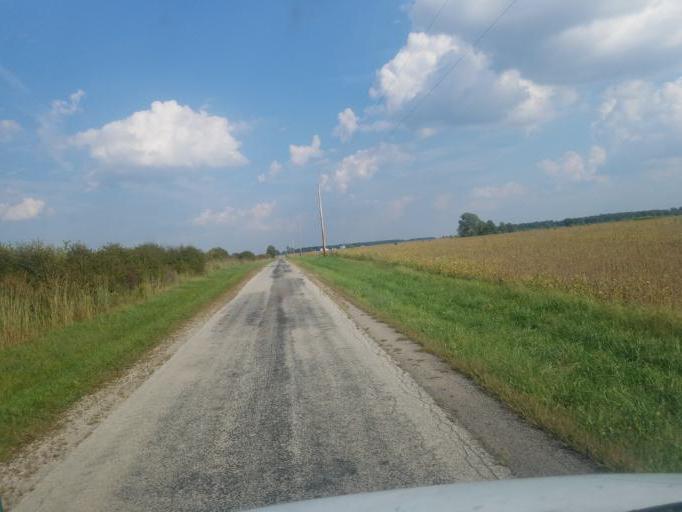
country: US
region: Ohio
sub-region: Hancock County
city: Arlington
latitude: 40.8194
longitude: -83.6277
